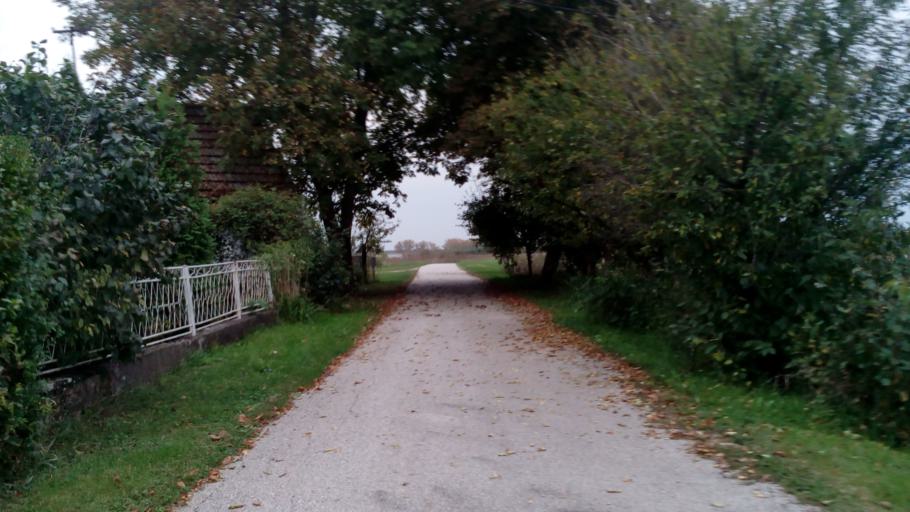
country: HR
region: Vukovarsko-Srijemska
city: Vinkovci
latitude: 45.2687
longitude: 18.8162
